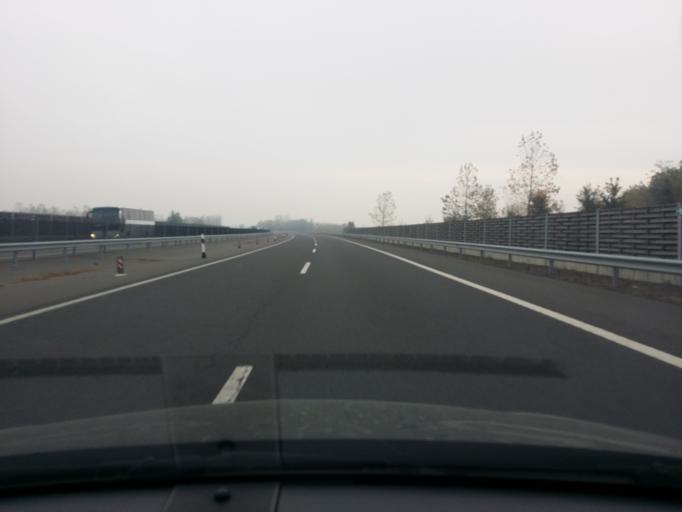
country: HU
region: Szabolcs-Szatmar-Bereg
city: Kalmanhaza
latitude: 47.8963
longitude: 21.6090
